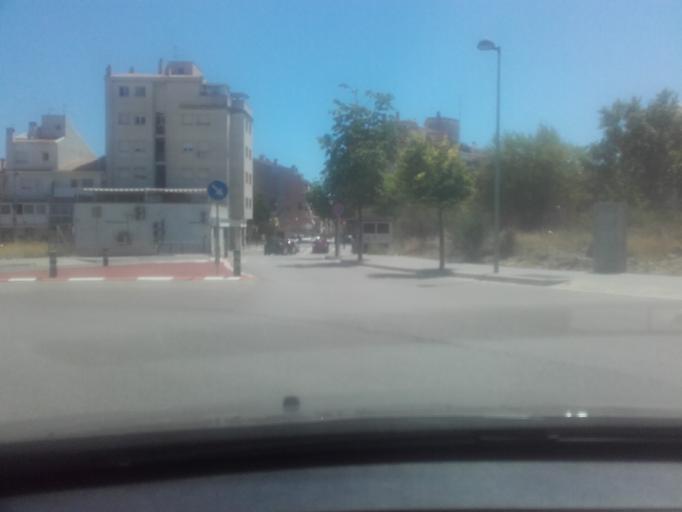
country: ES
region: Catalonia
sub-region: Provincia de Tarragona
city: El Vendrell
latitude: 41.2215
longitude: 1.5281
